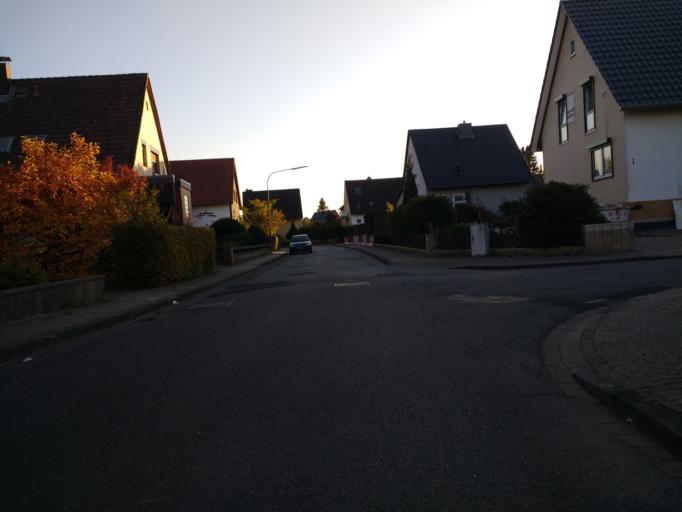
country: DE
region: Lower Saxony
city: Gifhorn
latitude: 52.4854
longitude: 10.5603
